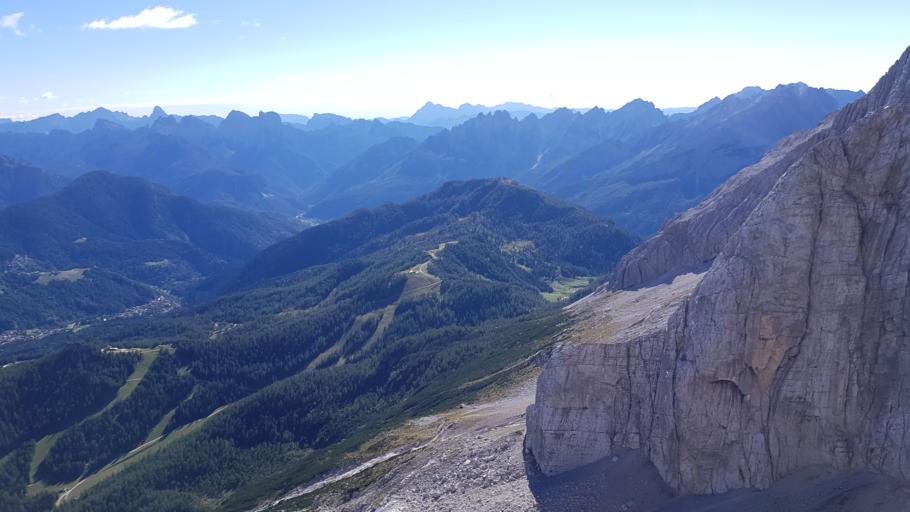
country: IT
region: Veneto
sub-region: Provincia di Belluno
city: Alleghe
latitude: 46.3844
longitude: 12.0600
